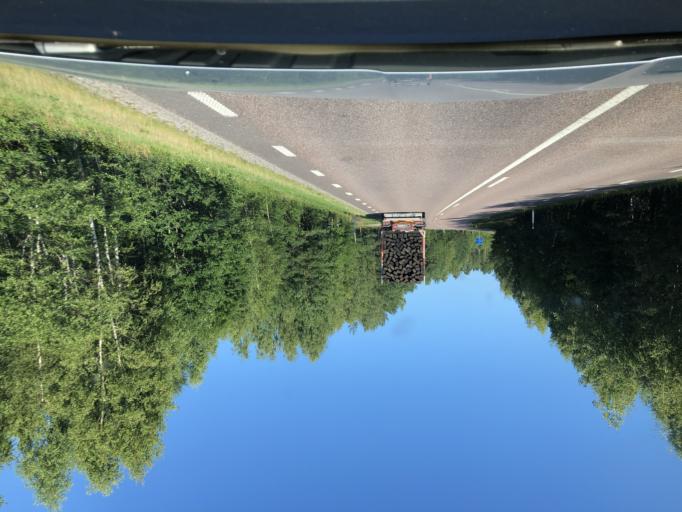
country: SE
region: Dalarna
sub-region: Faluns Kommun
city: Falun
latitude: 60.5792
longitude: 15.7739
